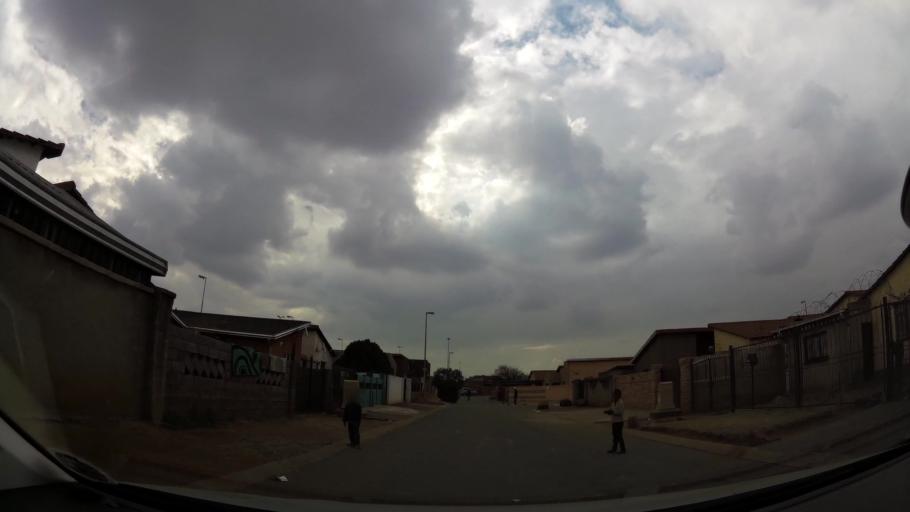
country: ZA
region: Gauteng
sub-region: City of Johannesburg Metropolitan Municipality
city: Soweto
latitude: -26.2597
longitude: 27.8566
